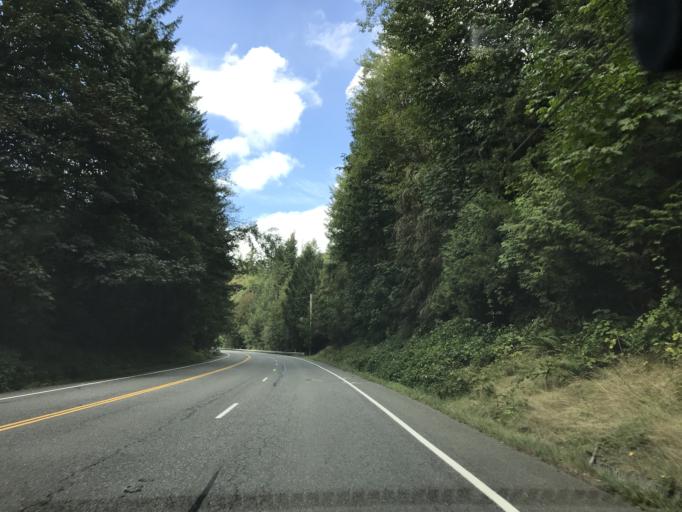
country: US
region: Washington
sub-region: King County
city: Black Diamond
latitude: 47.2889
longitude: -122.0506
